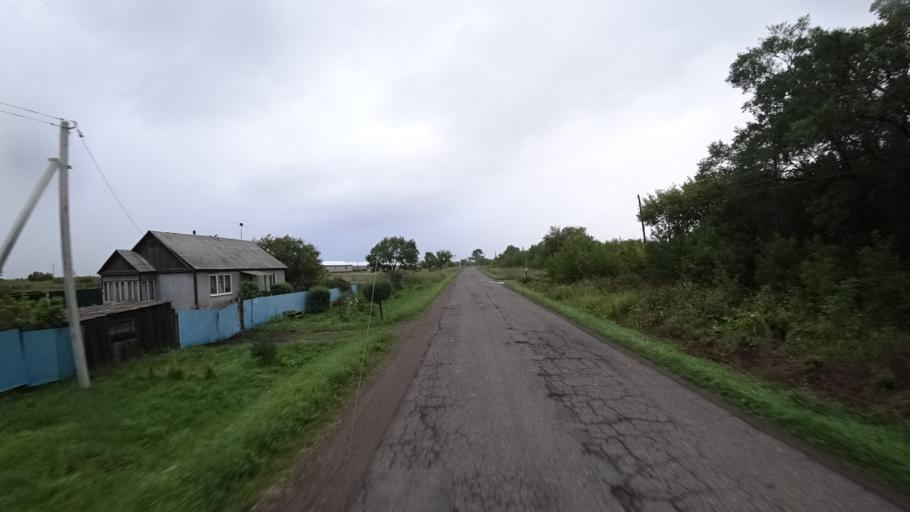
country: RU
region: Primorskiy
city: Chernigovka
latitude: 44.3977
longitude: 132.5277
